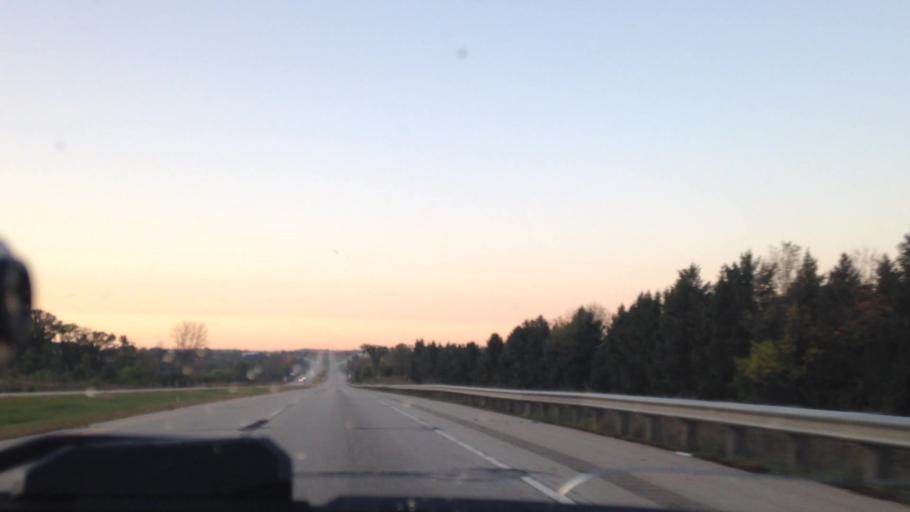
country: US
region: Wisconsin
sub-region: Dodge County
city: Theresa
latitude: 43.4923
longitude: -88.3671
